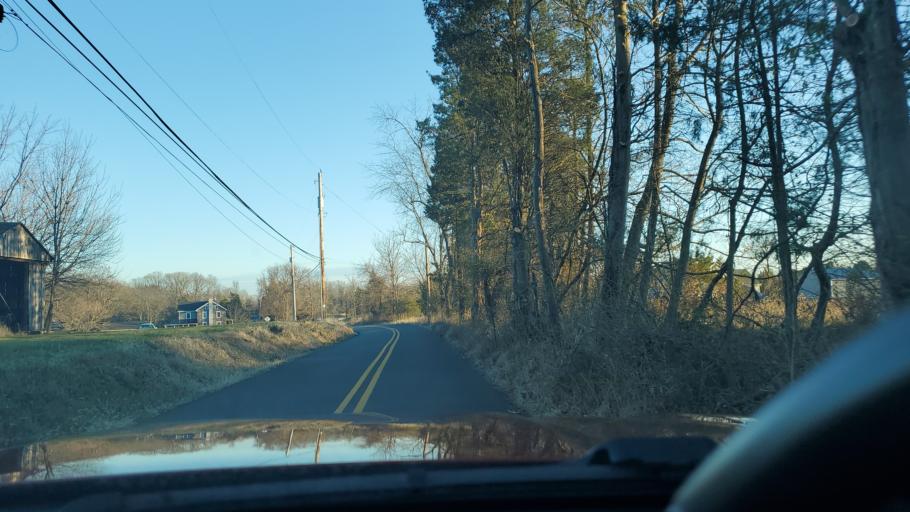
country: US
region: Pennsylvania
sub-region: Montgomery County
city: Woxall
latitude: 40.3122
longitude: -75.4940
